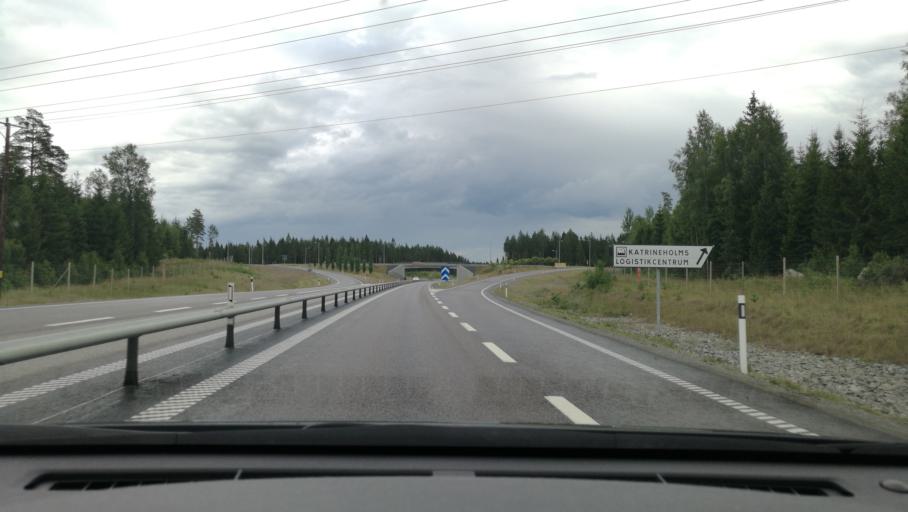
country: SE
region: Soedermanland
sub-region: Katrineholms Kommun
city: Katrineholm
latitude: 58.9960
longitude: 16.2571
